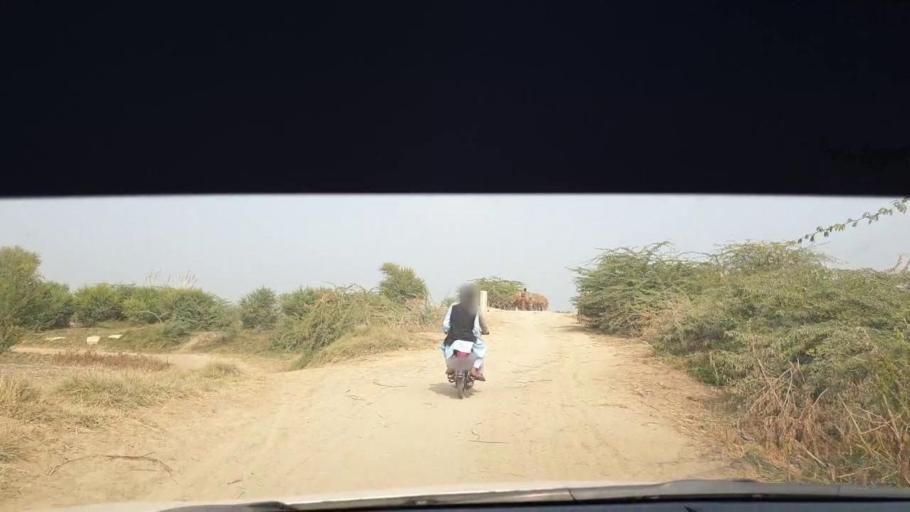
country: PK
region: Sindh
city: Berani
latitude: 25.8090
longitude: 68.8387
